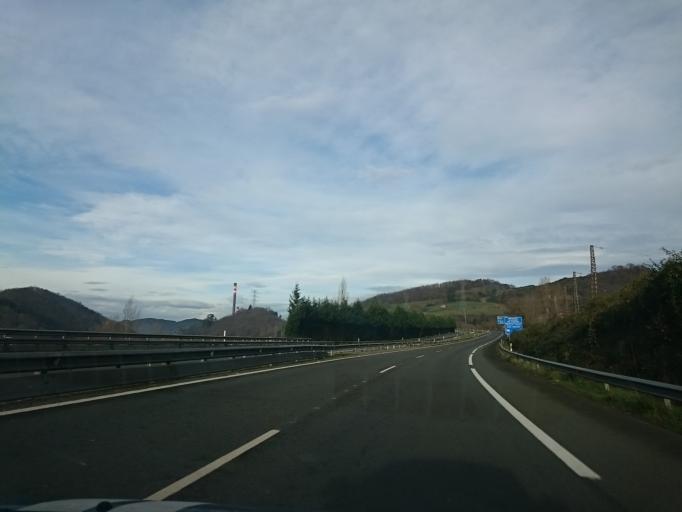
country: ES
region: Asturias
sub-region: Province of Asturias
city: Castandiello
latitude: 43.3087
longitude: -5.8598
